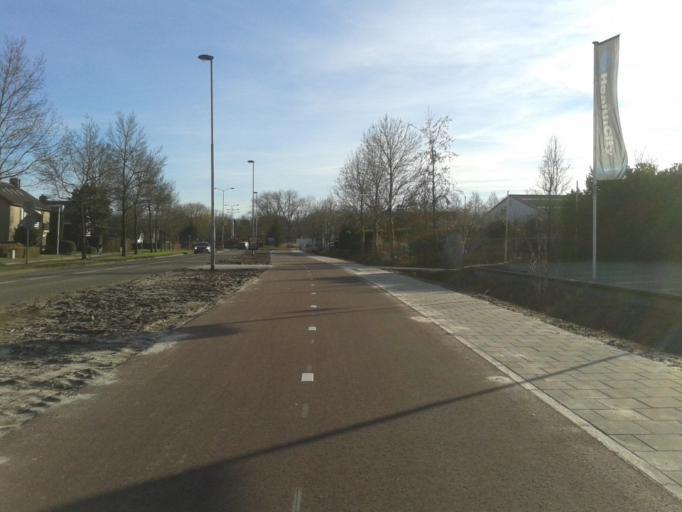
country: NL
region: North Brabant
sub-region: Gemeente Oisterwijk
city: Oisterwijk
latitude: 51.5732
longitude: 5.1822
